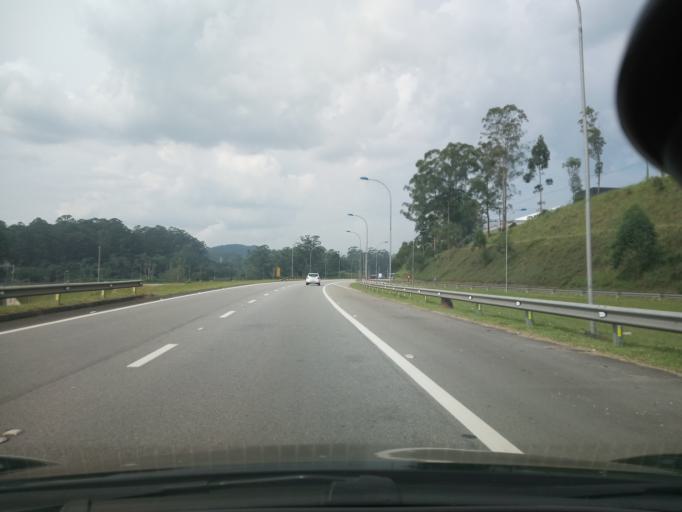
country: BR
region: Sao Paulo
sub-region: Sao Bernardo Do Campo
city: Sao Bernardo do Campo
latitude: -23.7652
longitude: -46.5881
